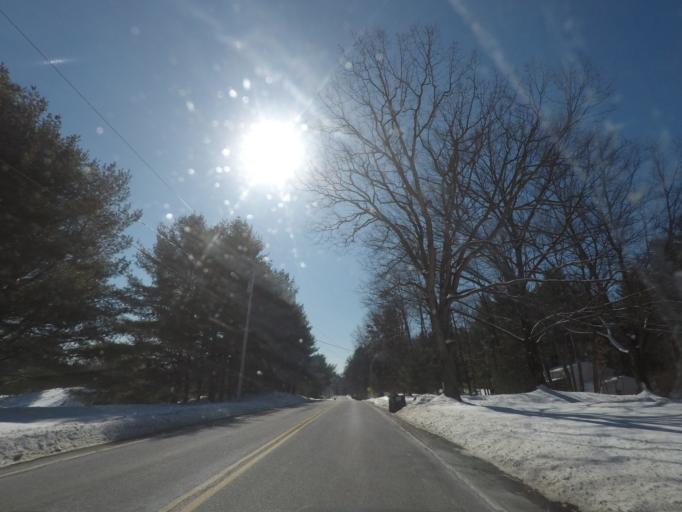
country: US
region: New York
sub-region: Saratoga County
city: Country Knolls
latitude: 42.9197
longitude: -73.8227
